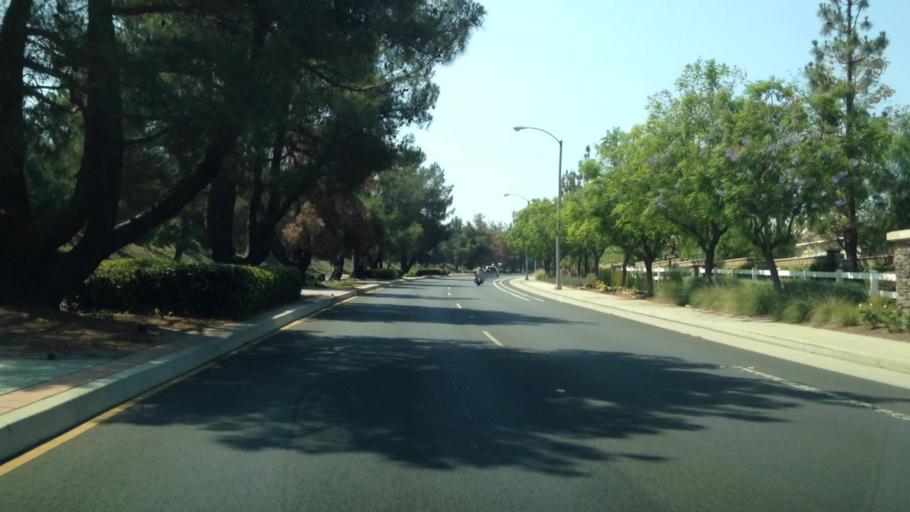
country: US
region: California
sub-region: Riverside County
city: Woodcrest
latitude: 33.8994
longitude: -117.3254
